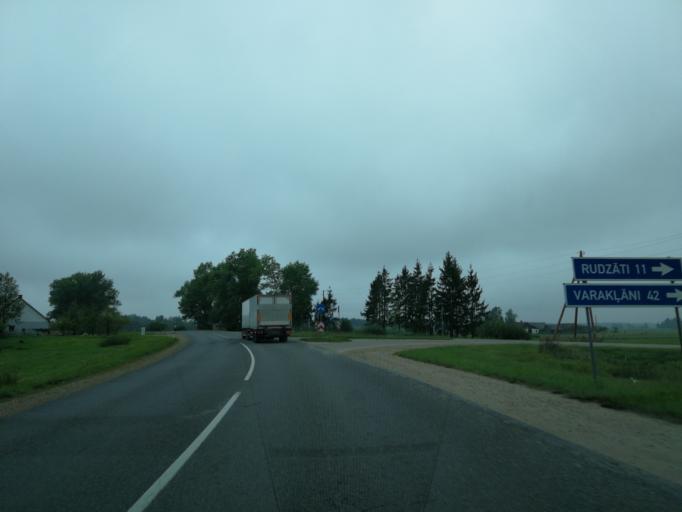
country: LV
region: Livani
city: Livani
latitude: 56.3414
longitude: 26.3560
